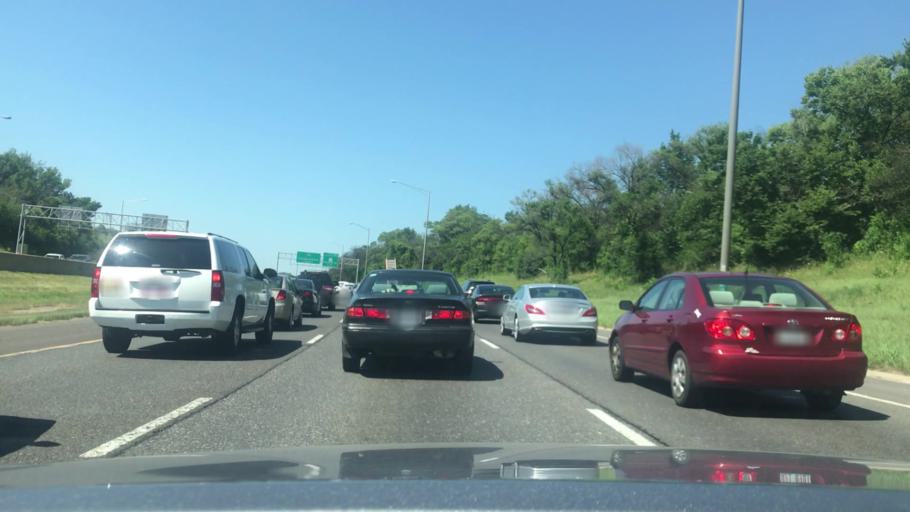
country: US
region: Illinois
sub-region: Cook County
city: Calumet Park
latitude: 41.7015
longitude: -87.6528
